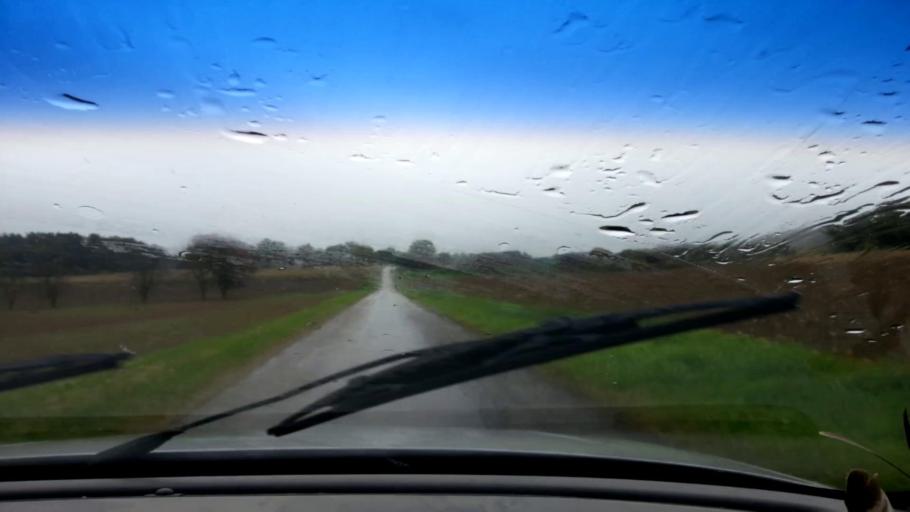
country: DE
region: Bavaria
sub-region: Upper Franconia
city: Heiligenstadt
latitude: 49.8835
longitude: 11.1518
